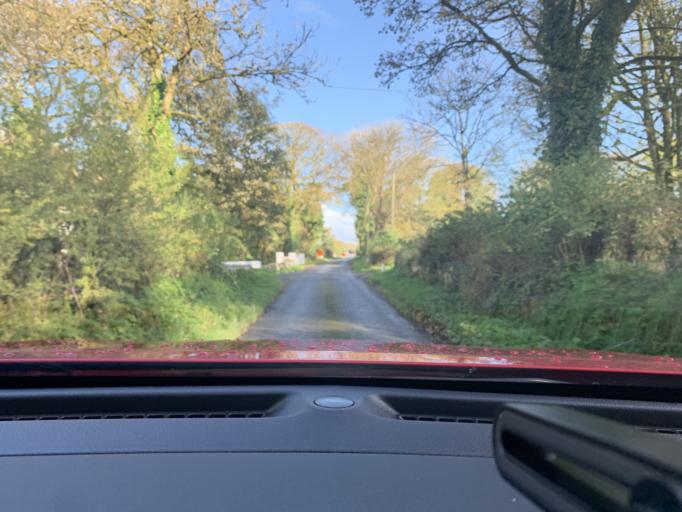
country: IE
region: Connaught
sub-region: Sligo
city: Ballymote
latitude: 54.1091
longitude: -8.4279
